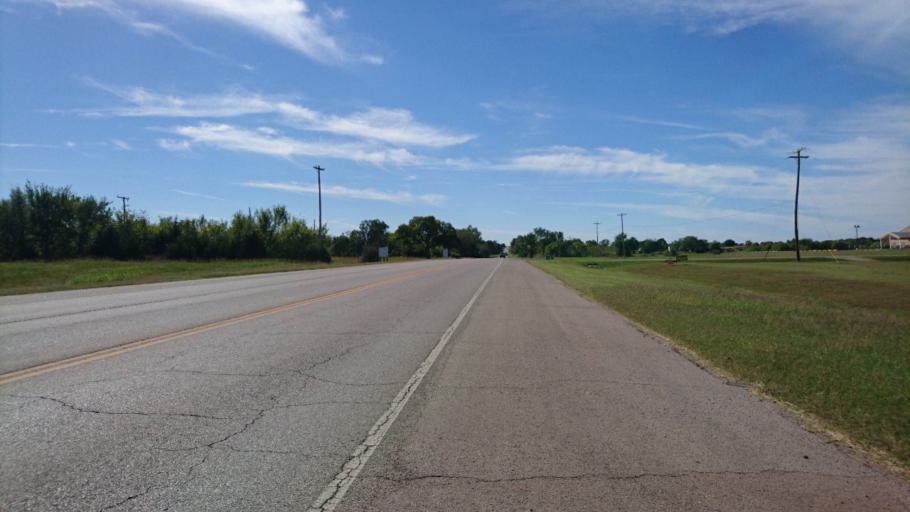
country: US
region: Oklahoma
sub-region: Lincoln County
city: Chandler
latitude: 35.7099
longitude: -96.7684
